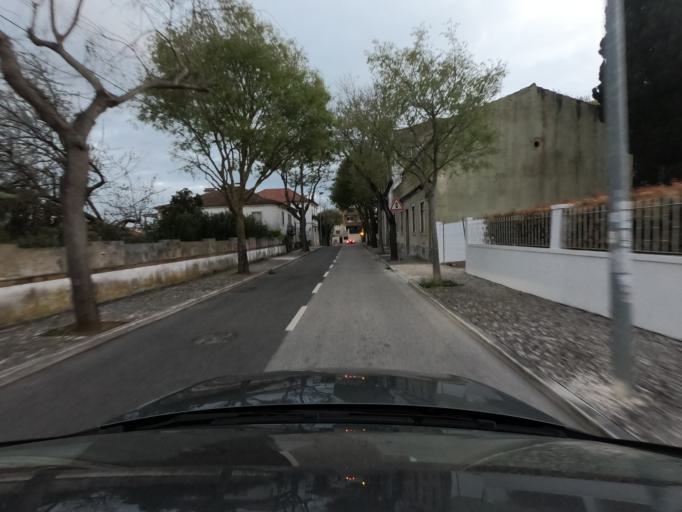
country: PT
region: Lisbon
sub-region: Oeiras
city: Terrugem
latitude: 38.7011
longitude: -9.2781
